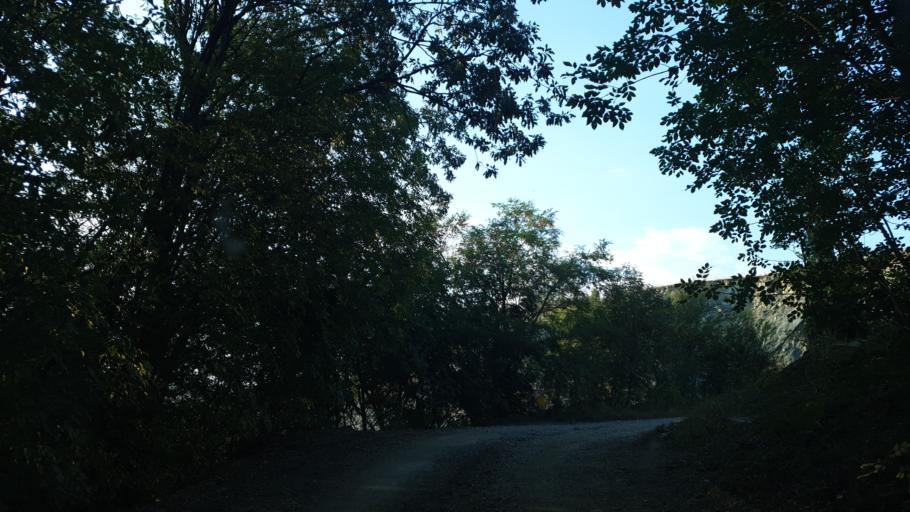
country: RS
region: Central Serbia
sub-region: Zlatiborski Okrug
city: Kosjeric
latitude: 43.9955
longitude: 20.0016
